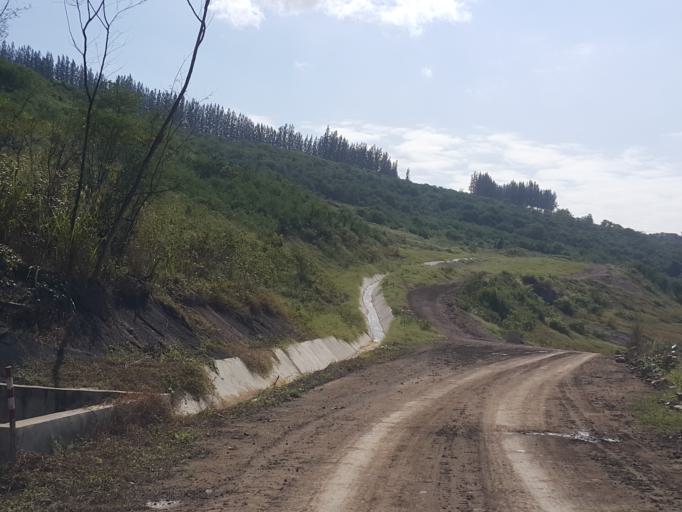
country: TH
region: Lampang
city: Mae Mo
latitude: 18.3240
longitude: 99.7377
